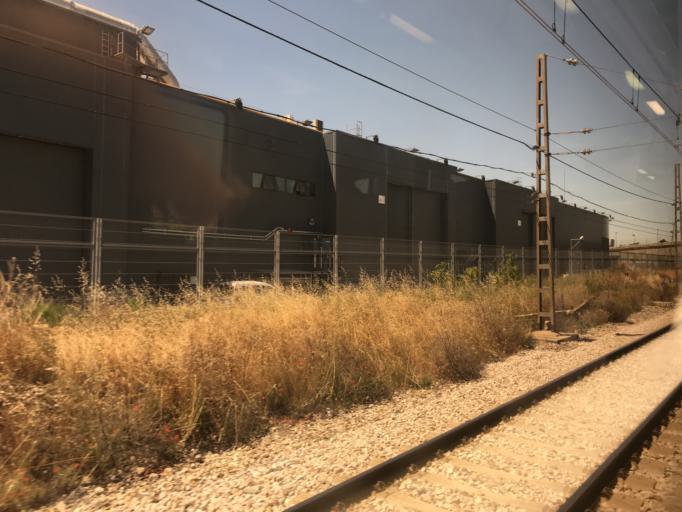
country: ES
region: Madrid
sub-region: Provincia de Madrid
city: Getafe
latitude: 40.3031
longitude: -3.7074
